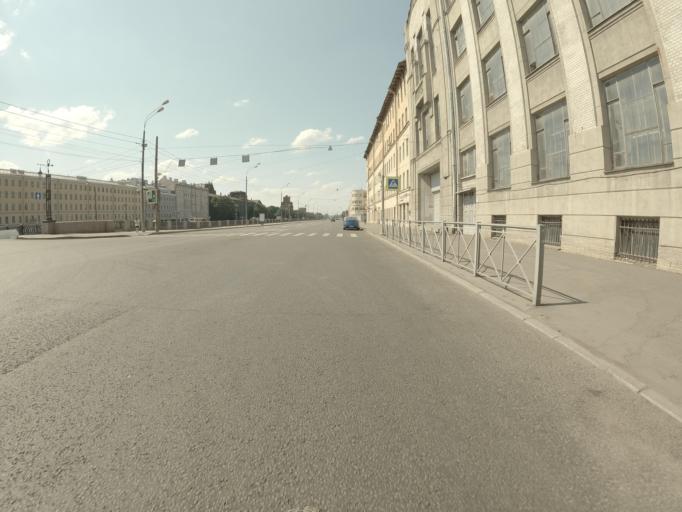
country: RU
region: St.-Petersburg
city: Admiralteisky
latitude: 59.9093
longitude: 30.2943
